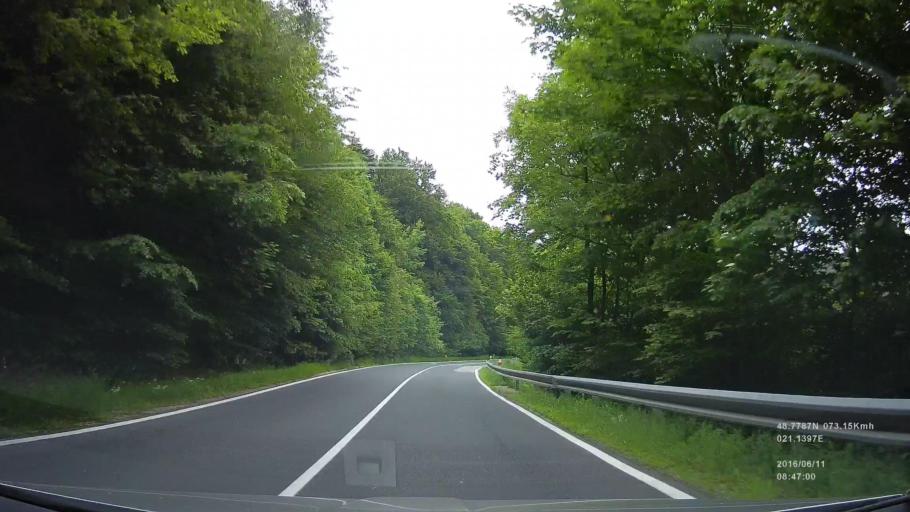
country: SK
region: Kosicky
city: Kosice
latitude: 48.7630
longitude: 21.1753
